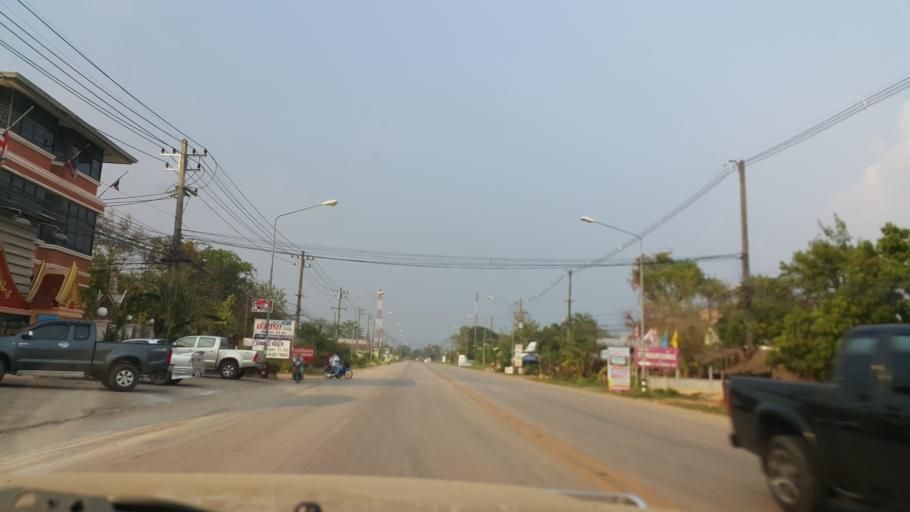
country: TH
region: Nakhon Phanom
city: That Phanom
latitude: 16.9502
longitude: 104.7218
